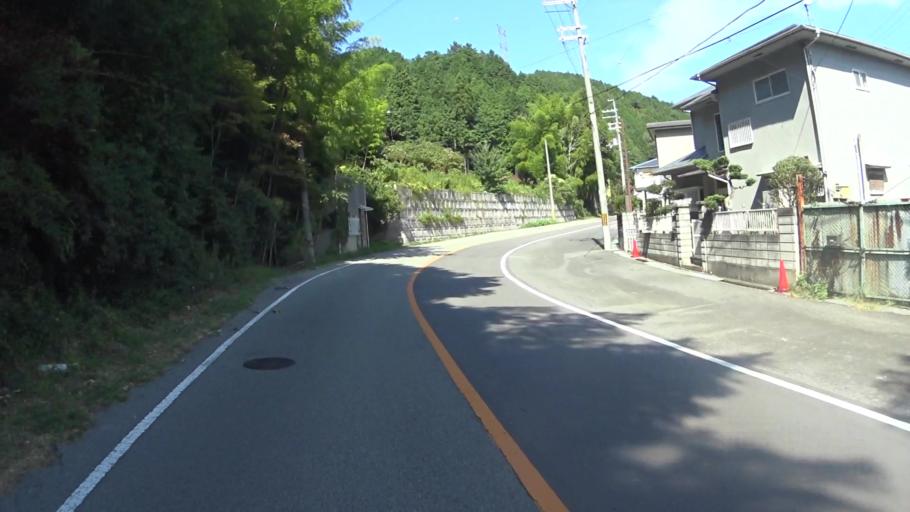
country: JP
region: Kyoto
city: Kameoka
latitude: 34.9716
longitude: 135.5058
